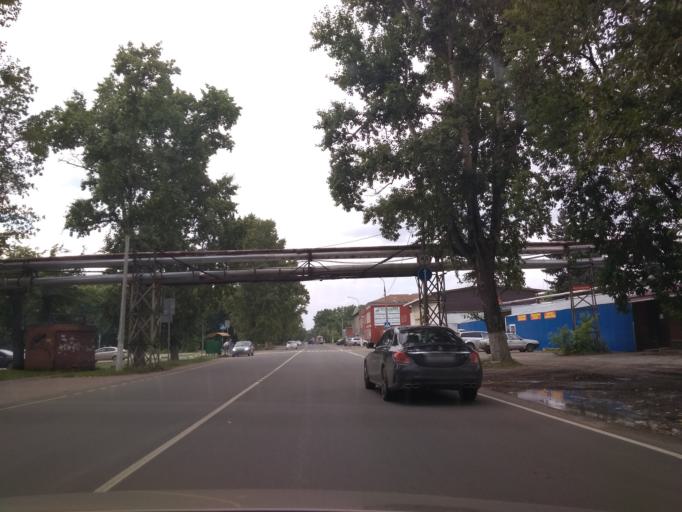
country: RU
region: Moskovskaya
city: Orekhovo-Zuyevo
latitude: 55.7977
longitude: 38.9437
